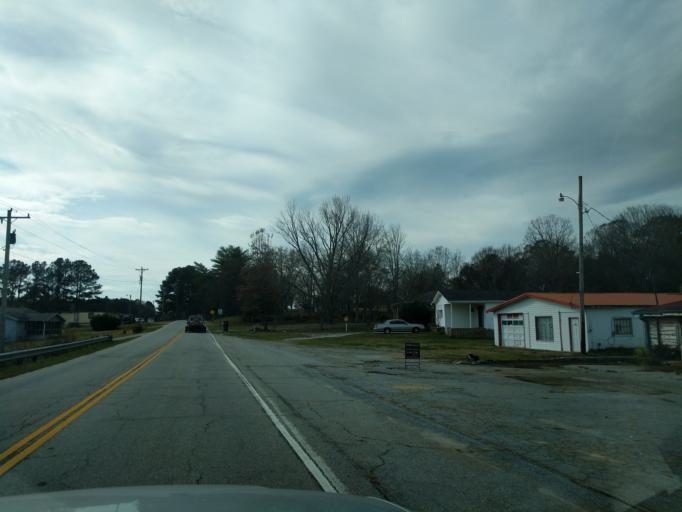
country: US
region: South Carolina
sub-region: Pickens County
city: Central
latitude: 34.8338
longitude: -82.8338
